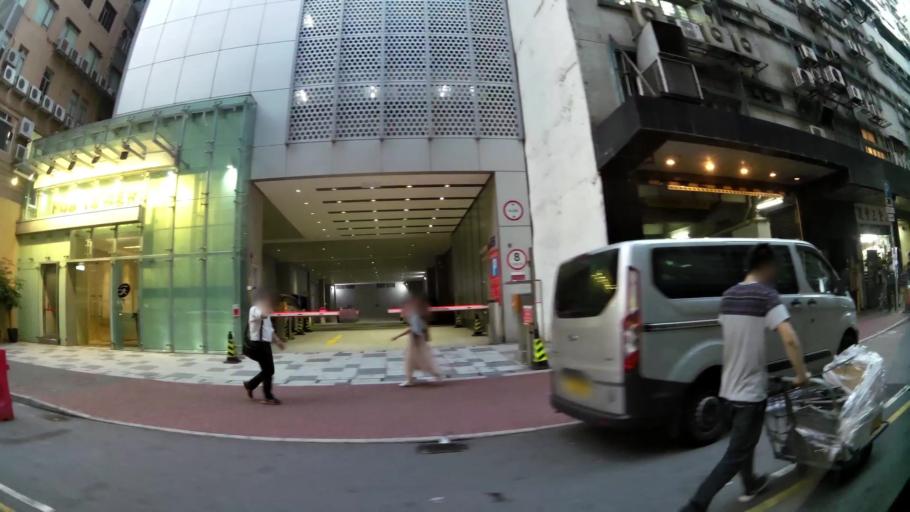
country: HK
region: Kowloon City
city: Kowloon
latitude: 22.3121
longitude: 114.2204
